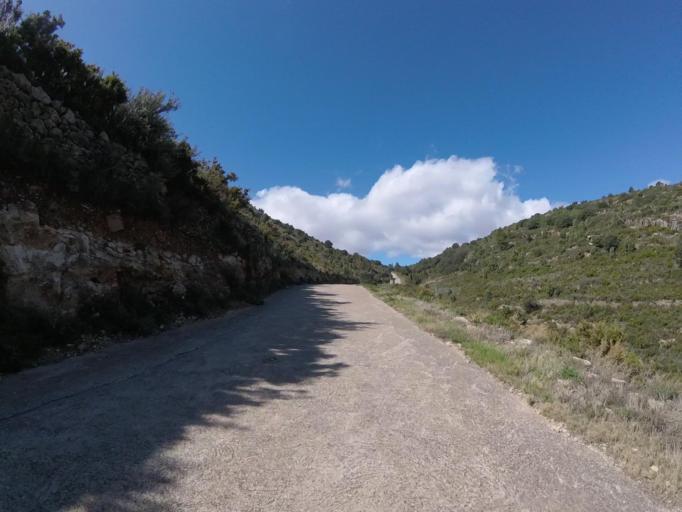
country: ES
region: Valencia
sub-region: Provincia de Castello
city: Culla
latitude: 40.3152
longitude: -0.0972
